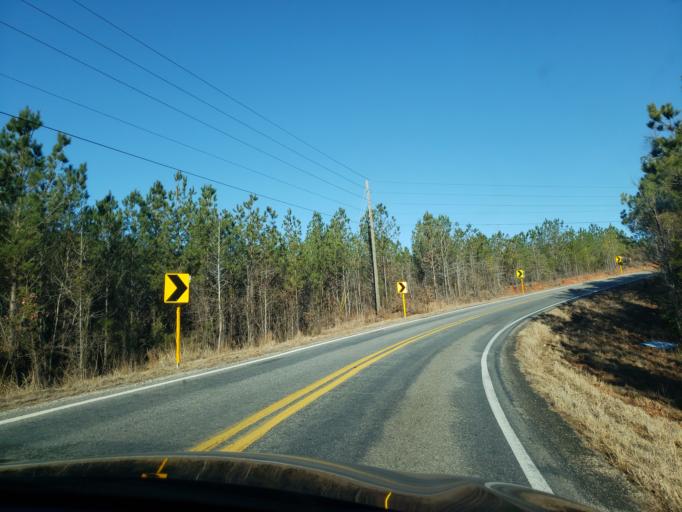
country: US
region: Alabama
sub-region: Elmore County
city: Tallassee
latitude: 32.6714
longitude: -85.8912
